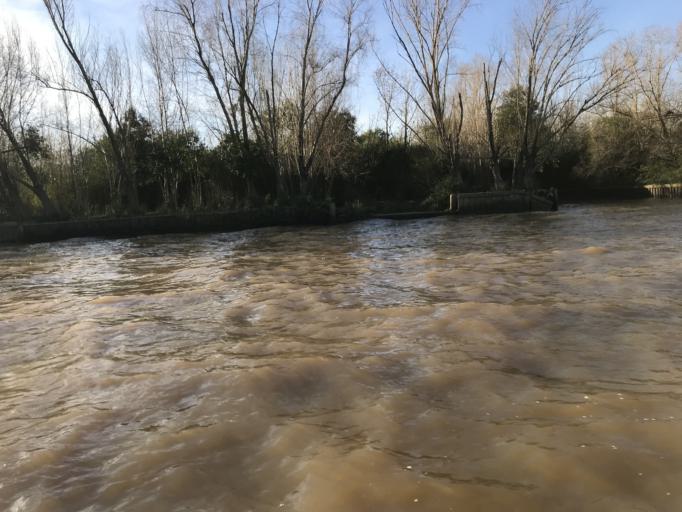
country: AR
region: Buenos Aires
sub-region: Partido de Tigre
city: Tigre
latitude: -34.4152
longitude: -58.5774
